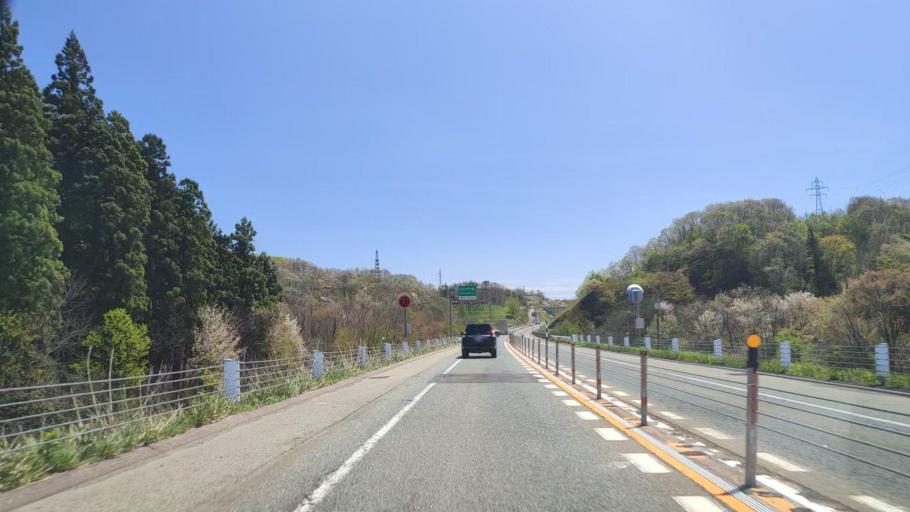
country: JP
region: Yamagata
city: Shinjo
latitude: 38.7280
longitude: 140.3063
